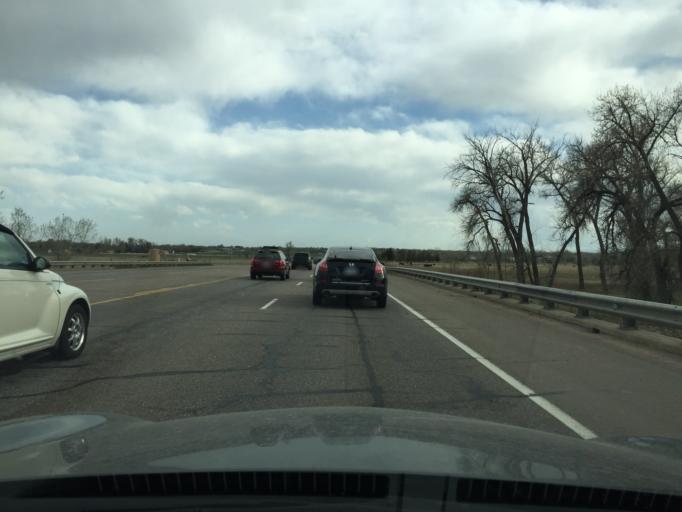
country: US
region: Colorado
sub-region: Boulder County
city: Erie
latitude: 40.0595
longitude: -105.1028
